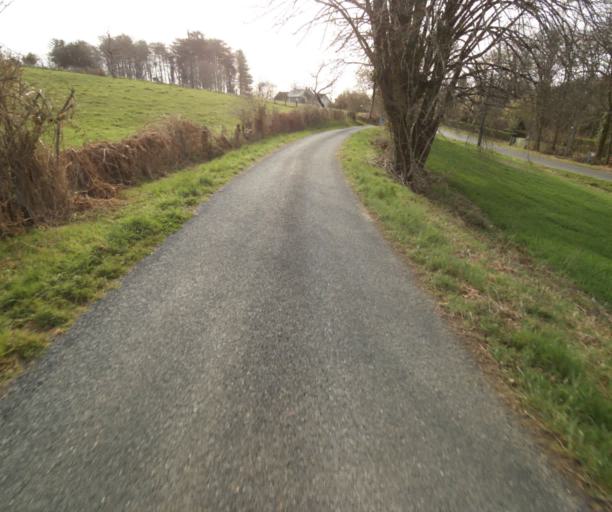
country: FR
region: Limousin
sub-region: Departement de la Correze
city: Chamboulive
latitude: 45.4335
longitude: 1.7649
